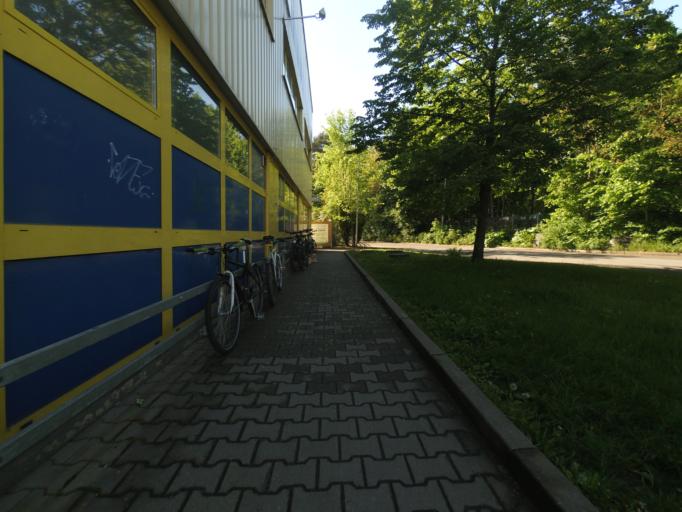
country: DE
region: Saxony
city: Dresden
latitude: 51.0160
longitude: 13.8054
